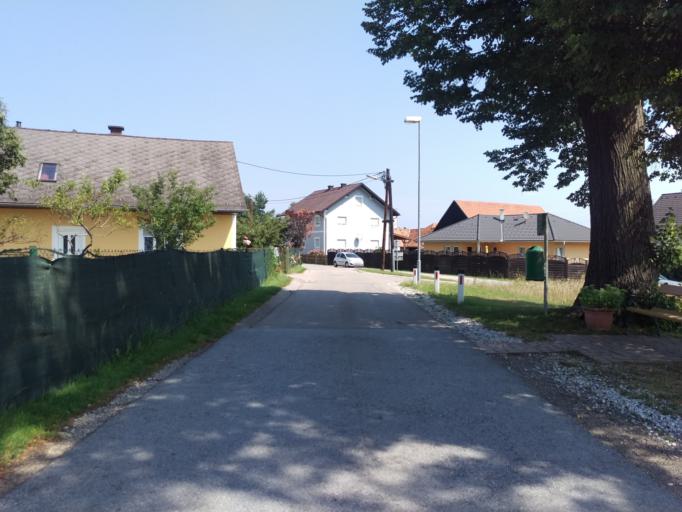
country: AT
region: Styria
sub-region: Politischer Bezirk Graz-Umgebung
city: Werndorf
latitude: 46.9424
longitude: 15.4876
